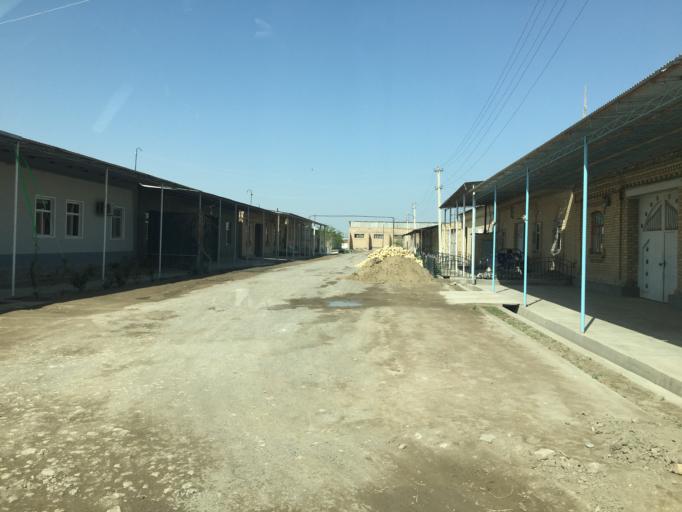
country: TM
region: Lebap
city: Turkmenabat
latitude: 38.9598
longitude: 63.6488
